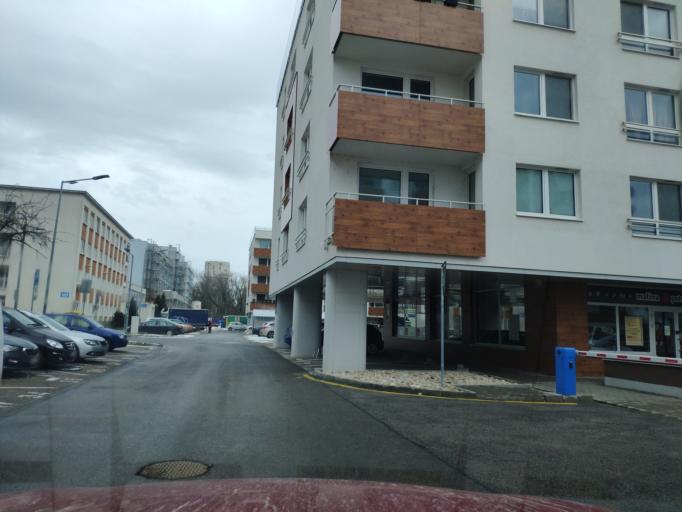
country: SK
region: Bratislavsky
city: Bratislava
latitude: 48.1818
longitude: 17.1361
